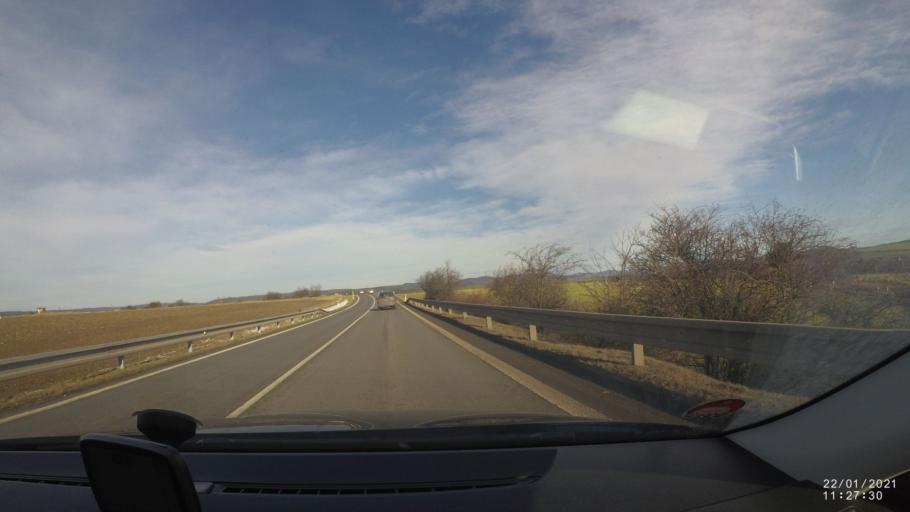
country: CZ
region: Central Bohemia
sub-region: Okres Beroun
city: Horovice
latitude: 49.8497
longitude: 13.9081
